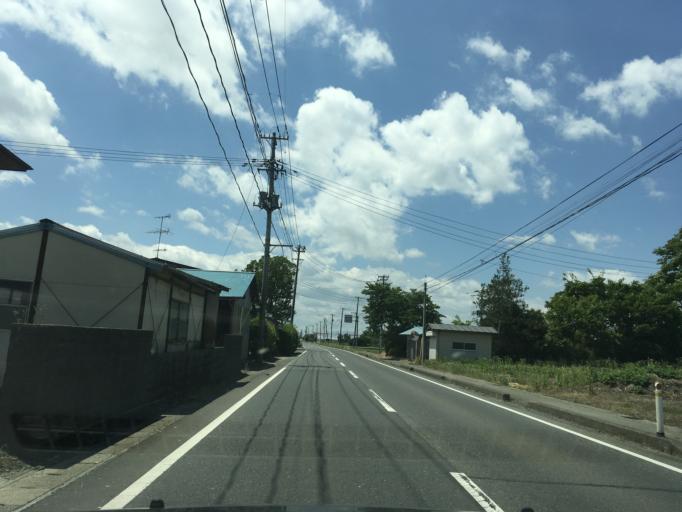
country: JP
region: Miyagi
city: Wakuya
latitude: 38.6768
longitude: 141.2469
